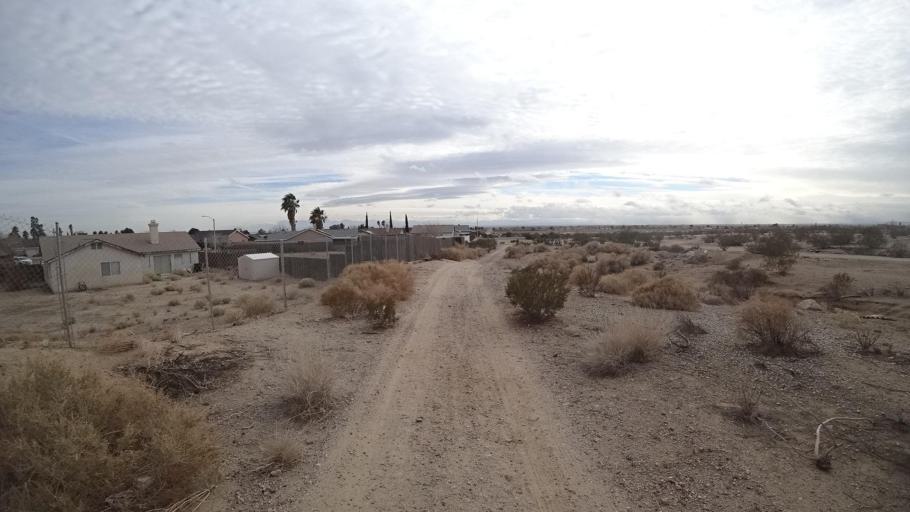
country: US
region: California
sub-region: Kern County
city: Rosamond
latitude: 34.8781
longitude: -118.1586
